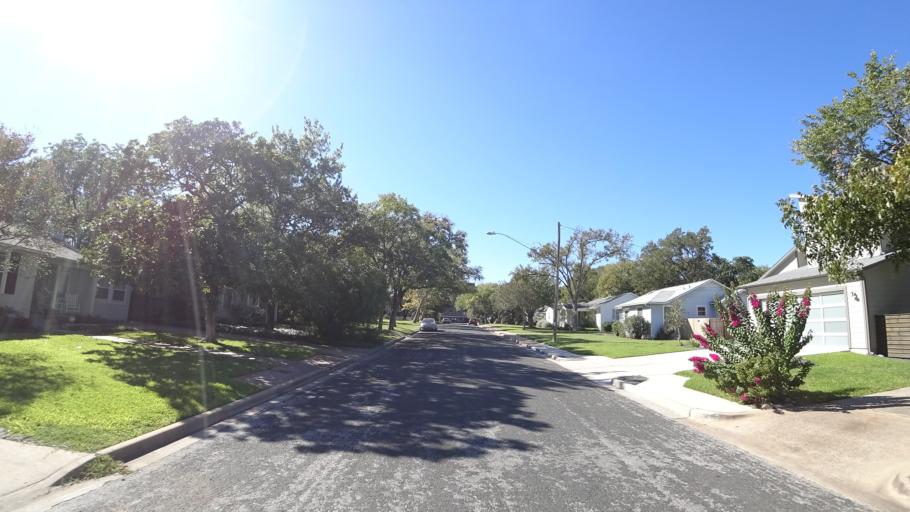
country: US
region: Texas
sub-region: Travis County
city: Austin
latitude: 30.3133
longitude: -97.7537
